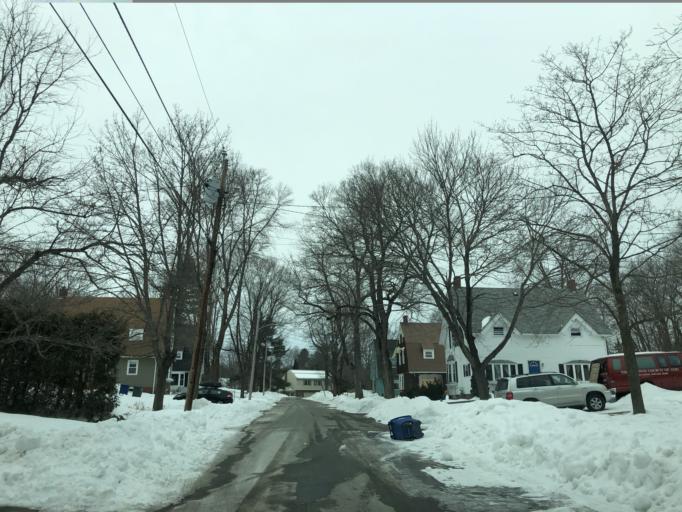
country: US
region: Maine
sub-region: Cumberland County
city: Westbrook
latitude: 43.6830
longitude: -70.3569
